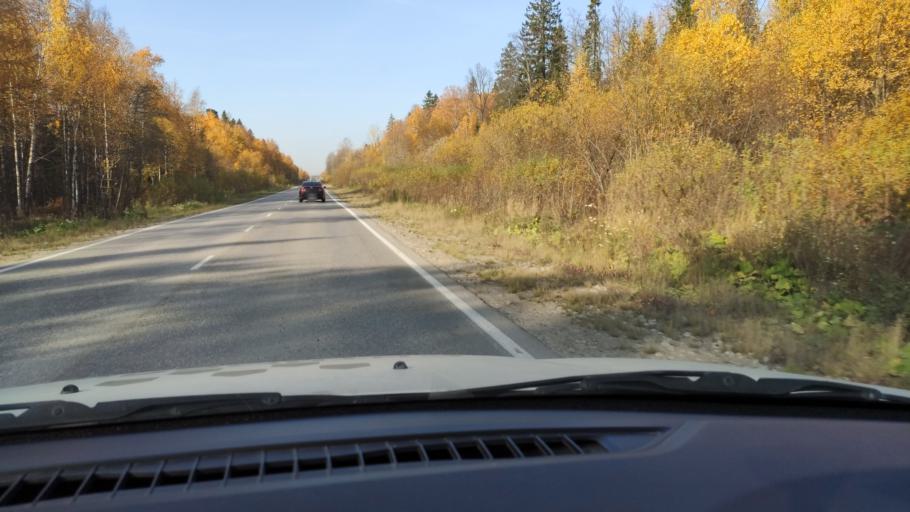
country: RU
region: Perm
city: Novyye Lyady
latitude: 58.0258
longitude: 56.6333
